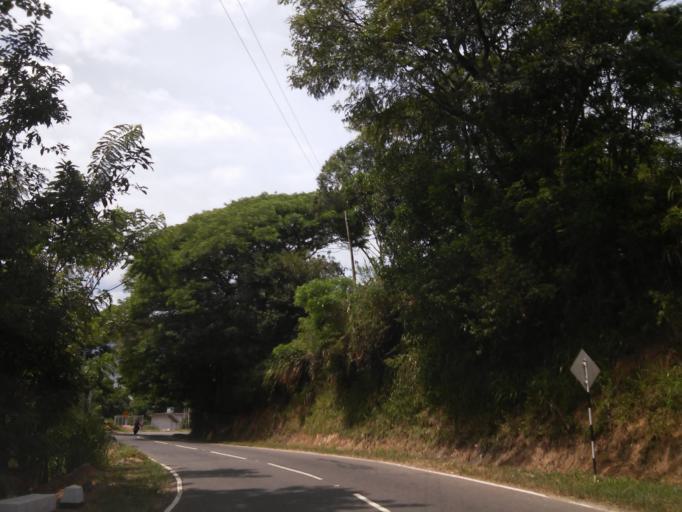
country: LK
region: Uva
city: Haputale
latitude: 6.8698
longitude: 80.9534
